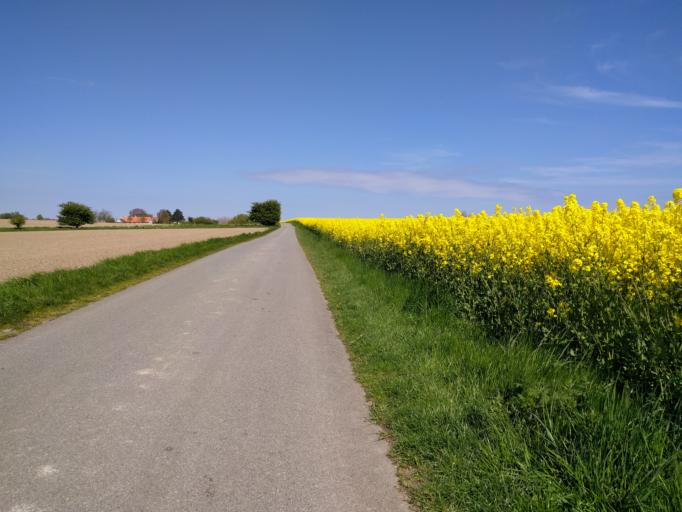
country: DK
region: South Denmark
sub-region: Kerteminde Kommune
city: Munkebo
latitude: 55.4484
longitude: 10.5897
